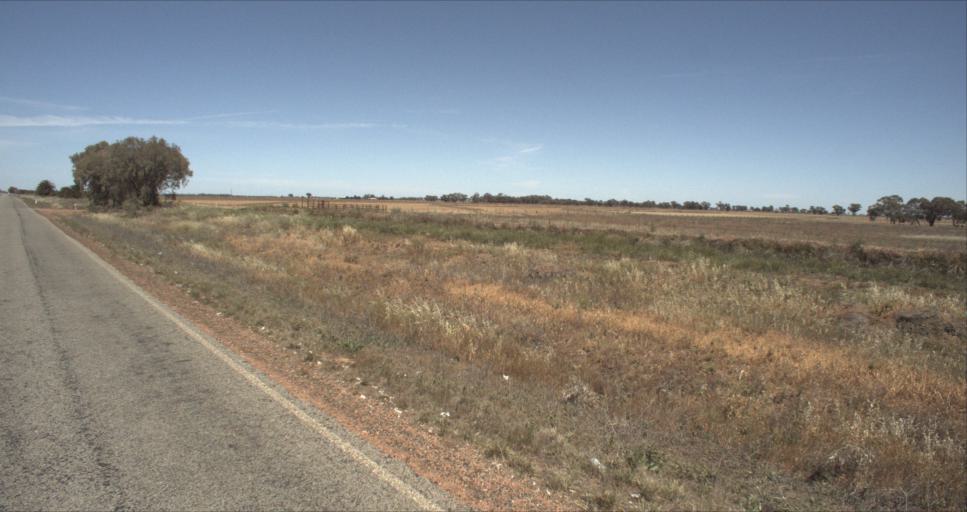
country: AU
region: New South Wales
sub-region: Leeton
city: Leeton
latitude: -34.4480
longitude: 146.2965
